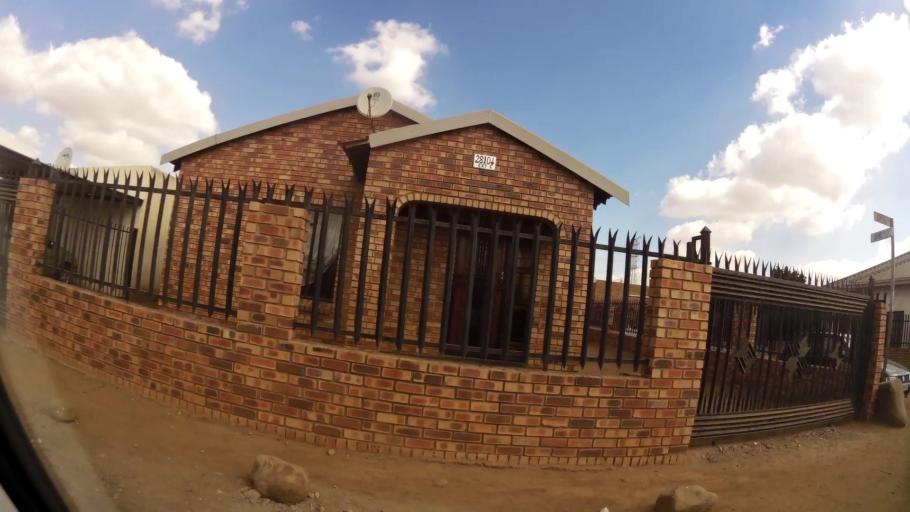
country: ZA
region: Gauteng
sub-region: City of Tshwane Metropolitan Municipality
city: Cullinan
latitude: -25.7070
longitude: 28.3975
